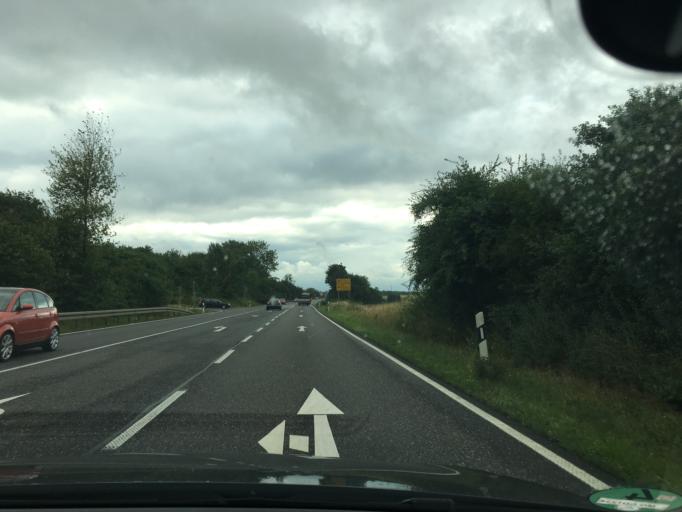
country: DE
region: North Rhine-Westphalia
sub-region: Regierungsbezirk Koln
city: Euskirchen
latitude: 50.6783
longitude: 6.7321
